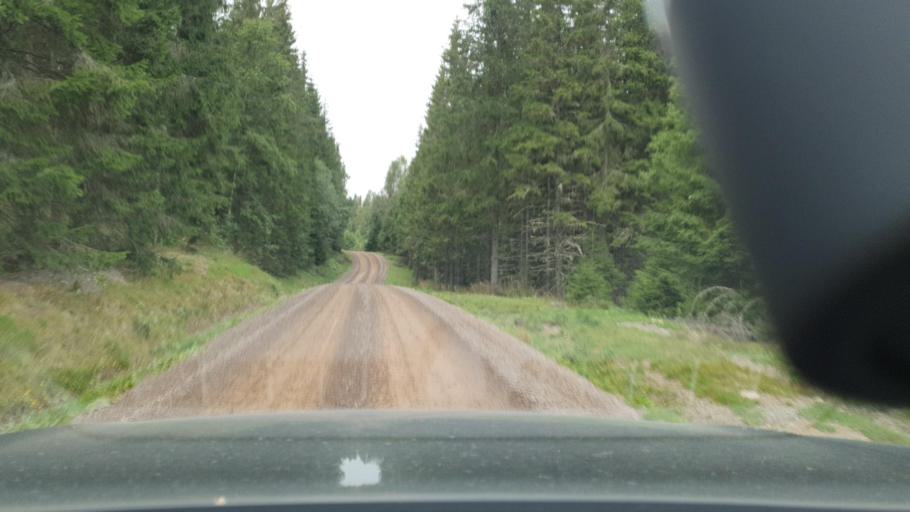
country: SE
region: Vaermland
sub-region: Eda Kommun
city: Charlottenberg
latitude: 60.0315
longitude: 12.6024
